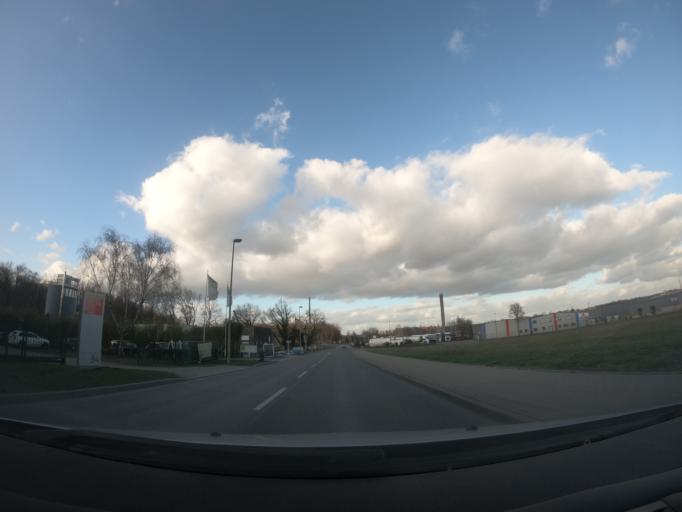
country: DE
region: North Rhine-Westphalia
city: Lunen
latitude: 51.5990
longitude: 7.4815
